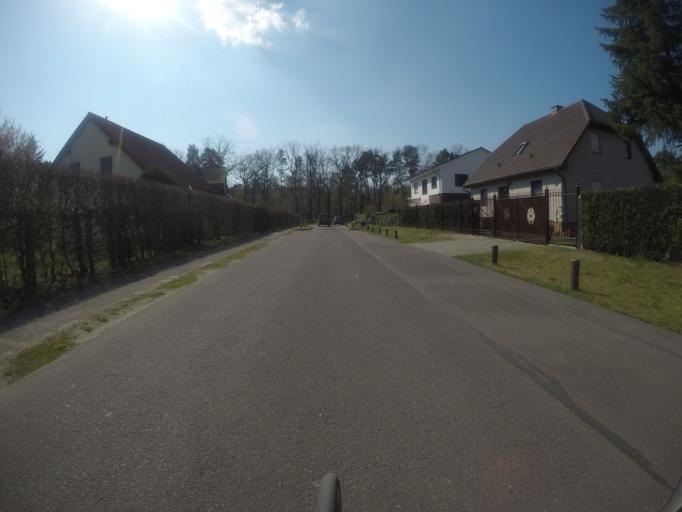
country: DE
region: Brandenburg
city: Hennigsdorf
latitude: 52.6396
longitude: 13.1875
